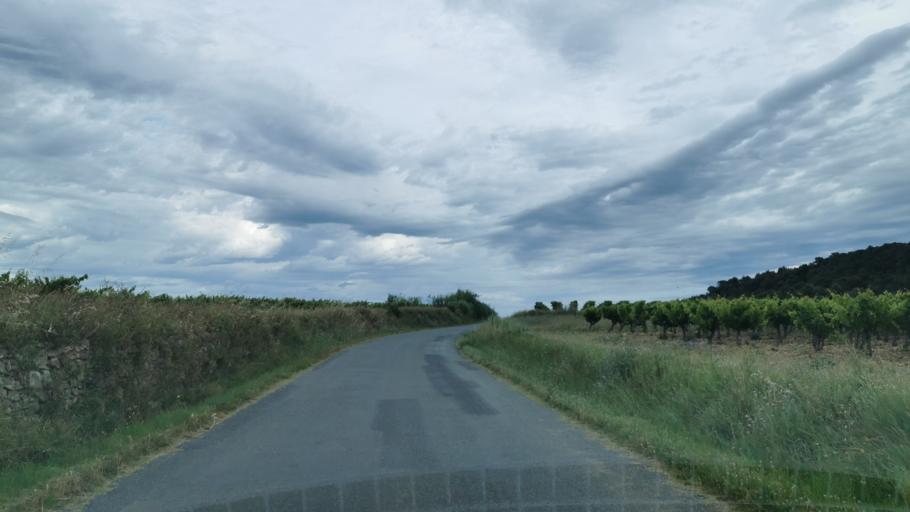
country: FR
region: Languedoc-Roussillon
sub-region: Departement de l'Aude
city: Moussan
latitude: 43.2235
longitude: 2.9385
